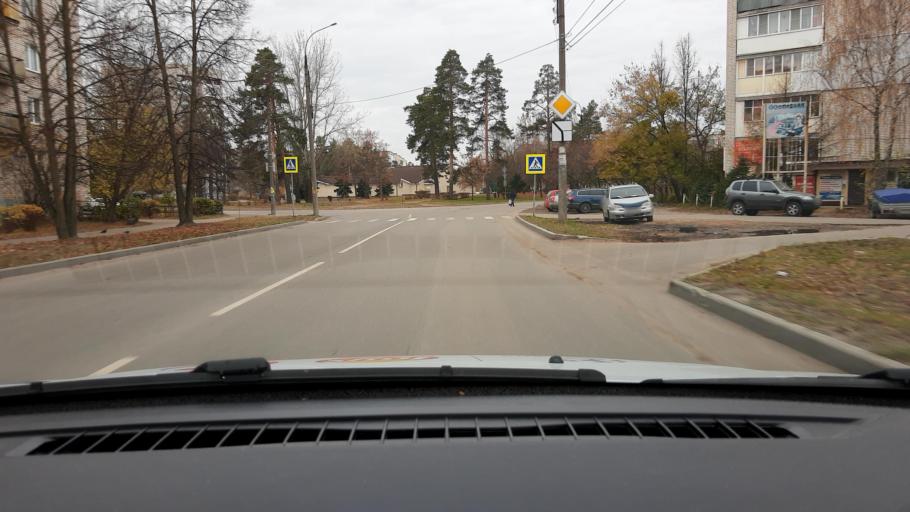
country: RU
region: Nizjnij Novgorod
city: Dzerzhinsk
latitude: 56.2513
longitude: 43.4484
